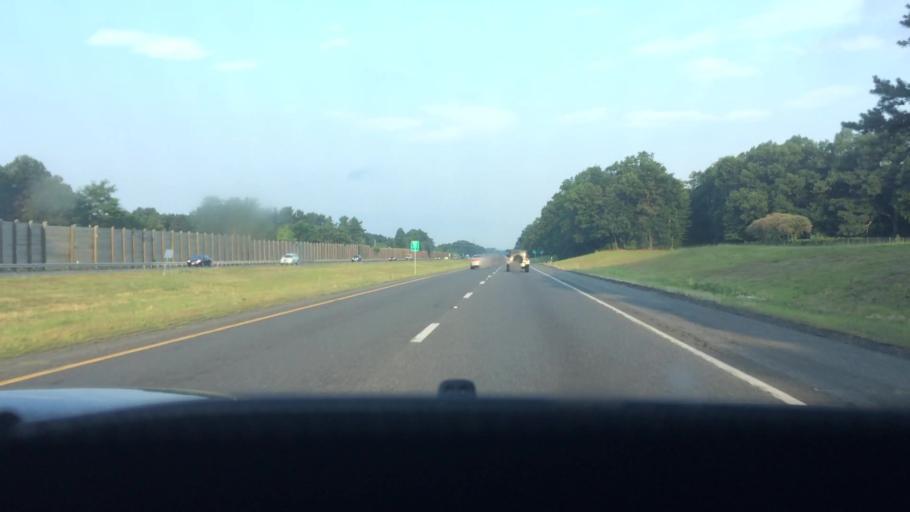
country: US
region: Massachusetts
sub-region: Hampden County
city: Ludlow
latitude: 42.1652
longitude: -72.5016
